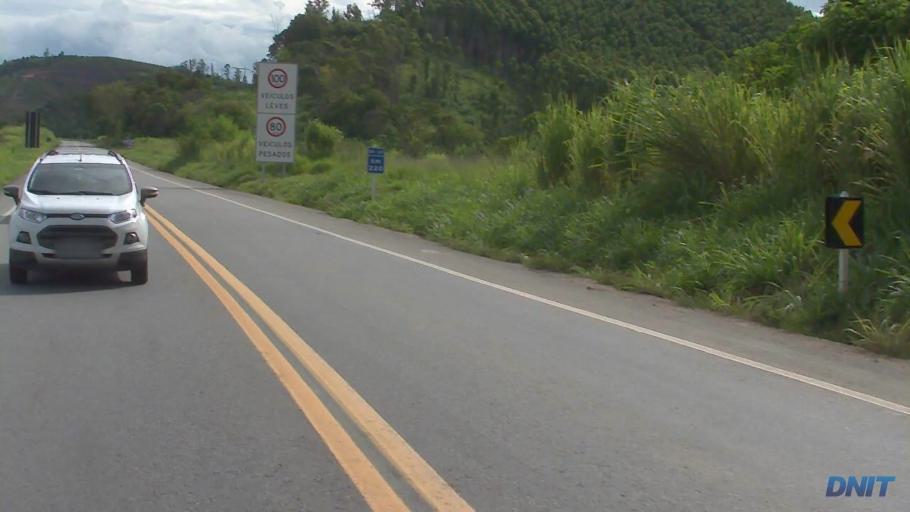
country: BR
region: Minas Gerais
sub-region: Belo Oriente
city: Belo Oriente
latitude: -19.2690
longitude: -42.3557
